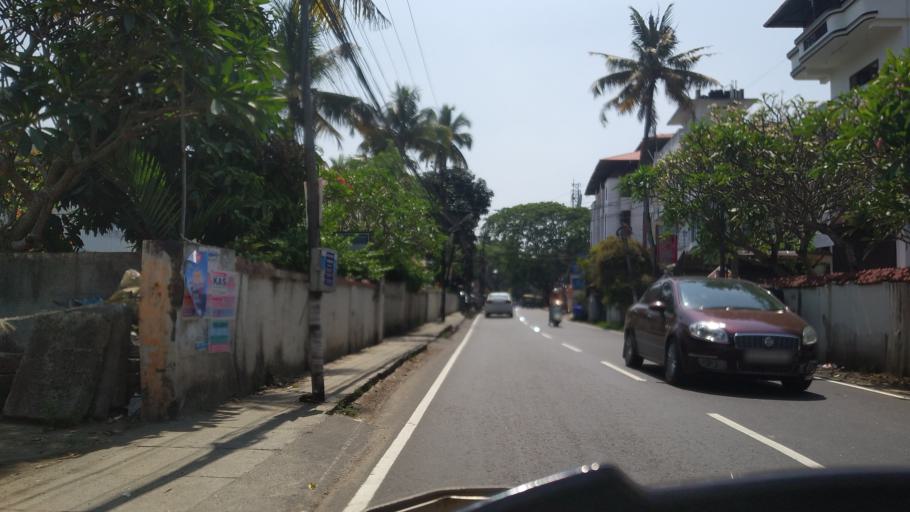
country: IN
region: Kerala
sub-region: Ernakulam
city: Cochin
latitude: 9.9958
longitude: 76.3080
